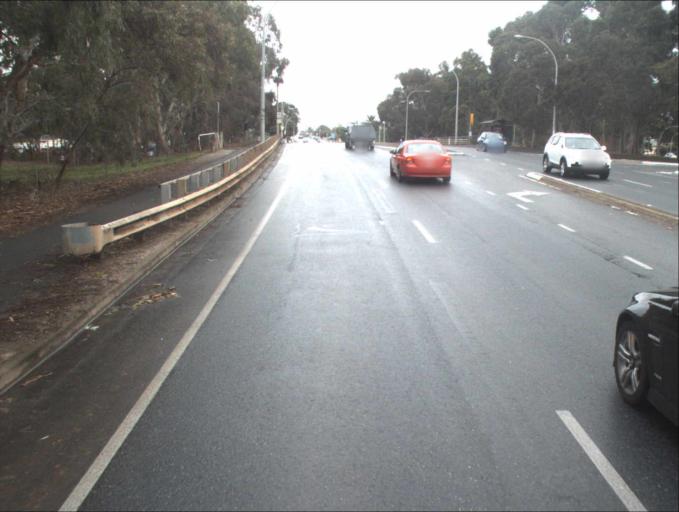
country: AU
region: South Australia
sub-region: Norwood Payneham St Peters
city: Marden
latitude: -34.8876
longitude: 138.6393
